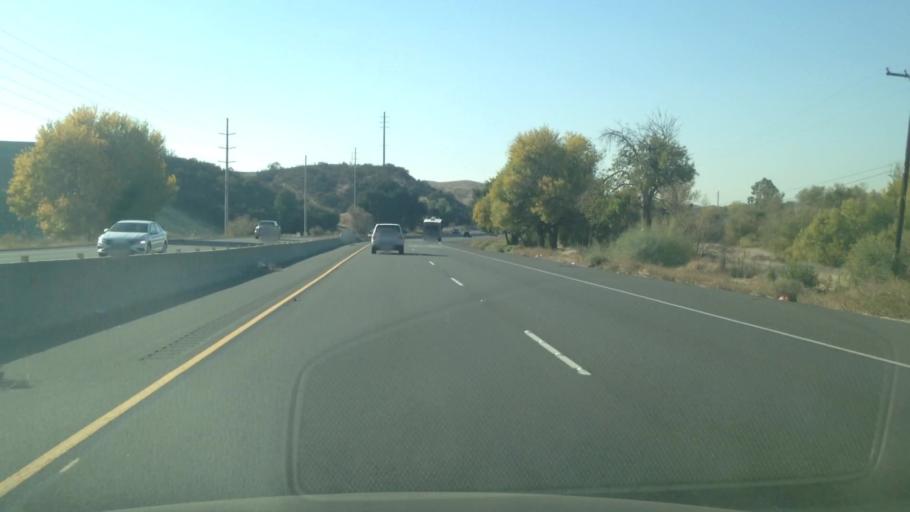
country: US
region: California
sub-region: Riverside County
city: Beaumont
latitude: 33.9328
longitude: -117.0275
